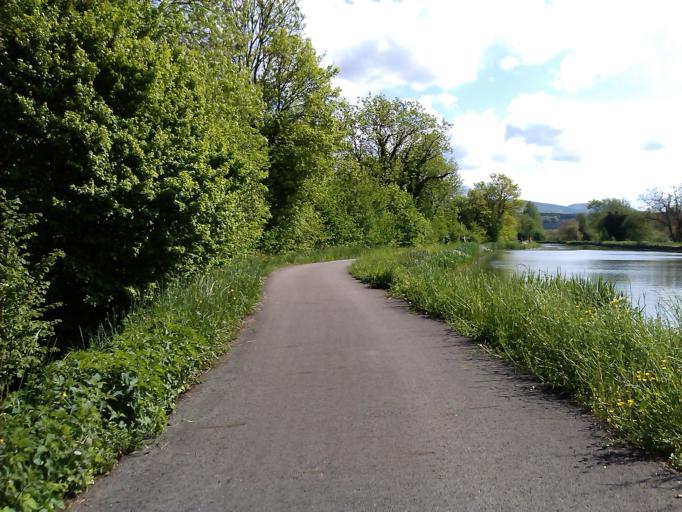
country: FR
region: Franche-Comte
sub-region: Departement du Doubs
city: Colombier-Fontaine
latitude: 47.4420
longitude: 6.6290
